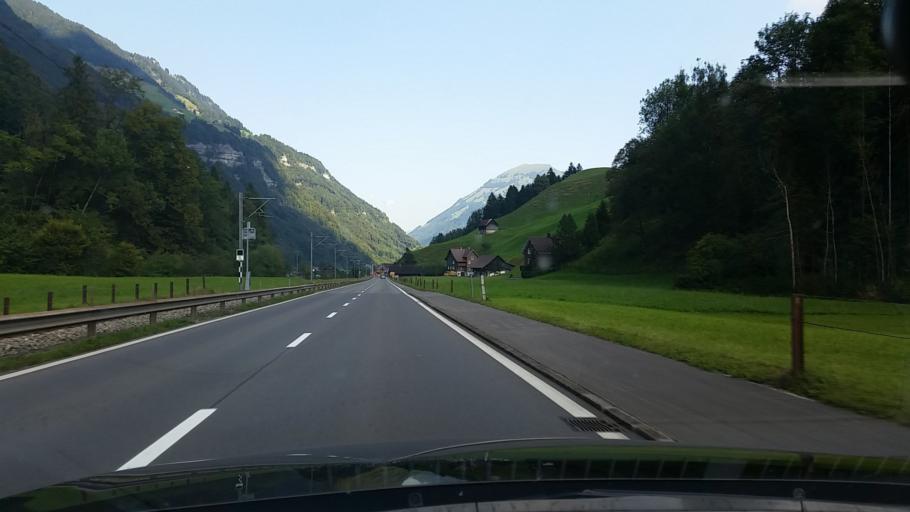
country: CH
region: Nidwalden
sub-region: Nidwalden
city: Wolfenschiessen
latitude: 46.8740
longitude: 8.3740
